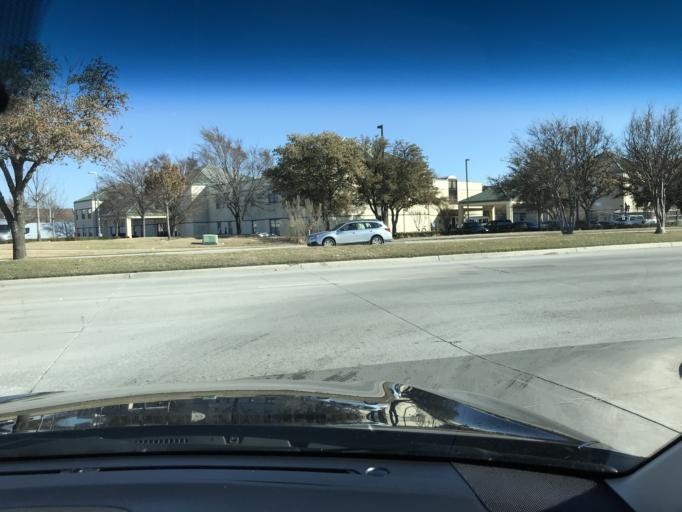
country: US
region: Texas
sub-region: Tarrant County
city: Benbrook
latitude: 32.6648
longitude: -97.4211
